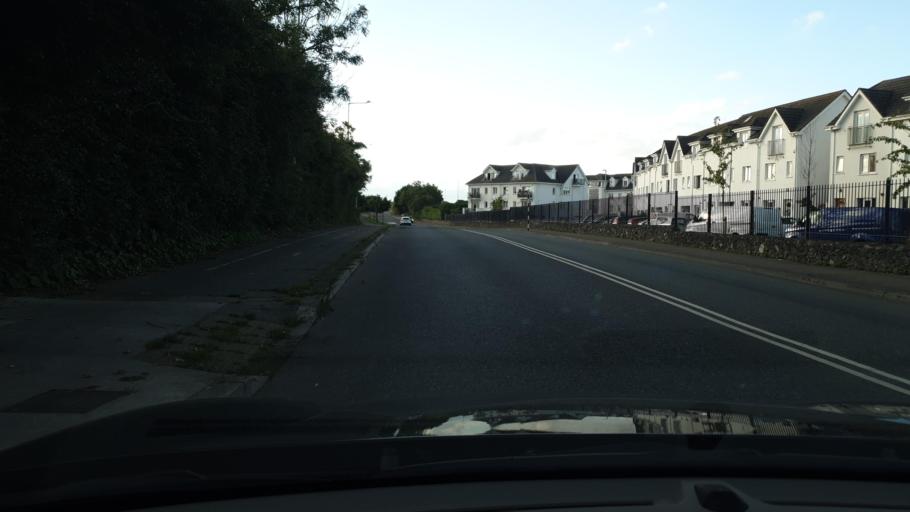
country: IE
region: Leinster
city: Balbriggan
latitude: 53.6171
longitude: -6.1939
